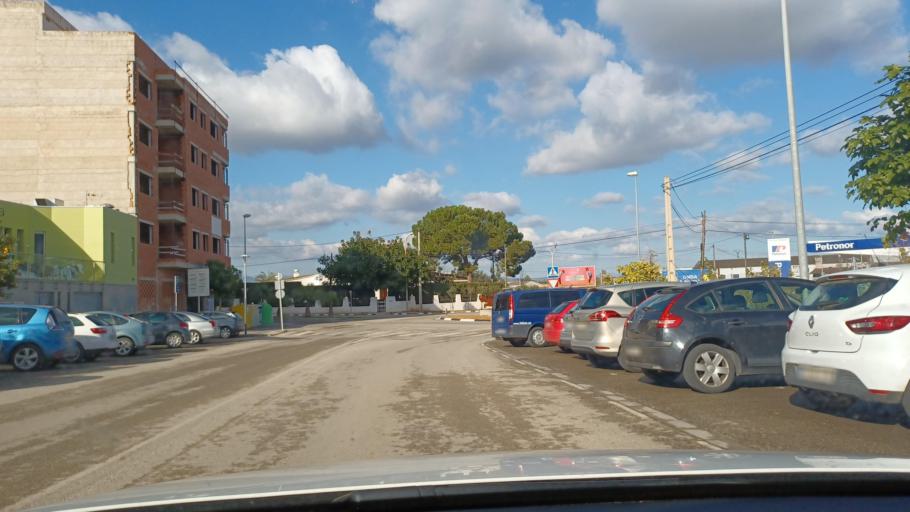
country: ES
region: Valencia
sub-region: Provincia de Castello
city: Betxi
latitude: 39.9304
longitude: -0.1969
